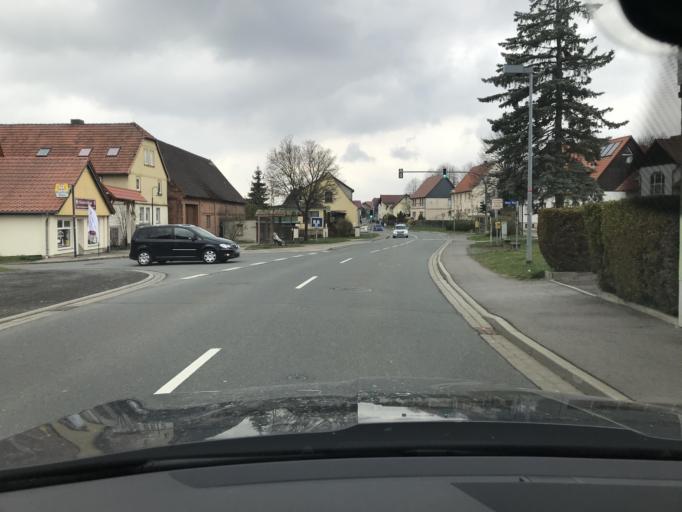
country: DE
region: Saxony-Anhalt
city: Harzgerode
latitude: 51.6024
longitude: 11.2044
